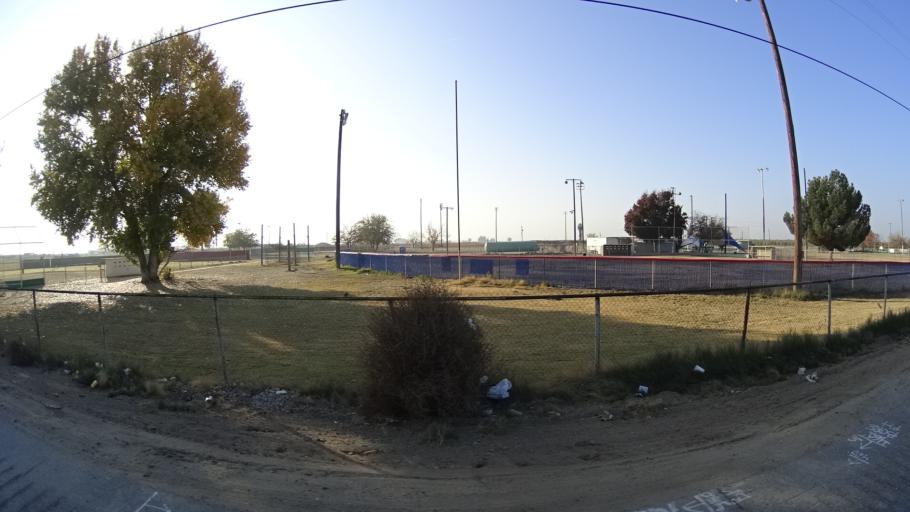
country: US
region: California
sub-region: Kern County
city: Greenfield
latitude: 35.2668
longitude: -118.9831
